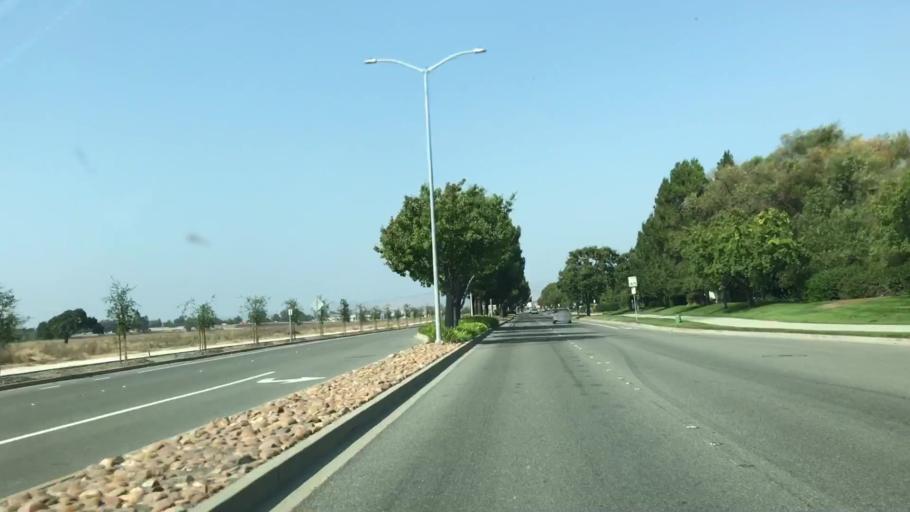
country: US
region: California
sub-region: Alameda County
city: Newark
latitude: 37.5559
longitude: -122.0672
